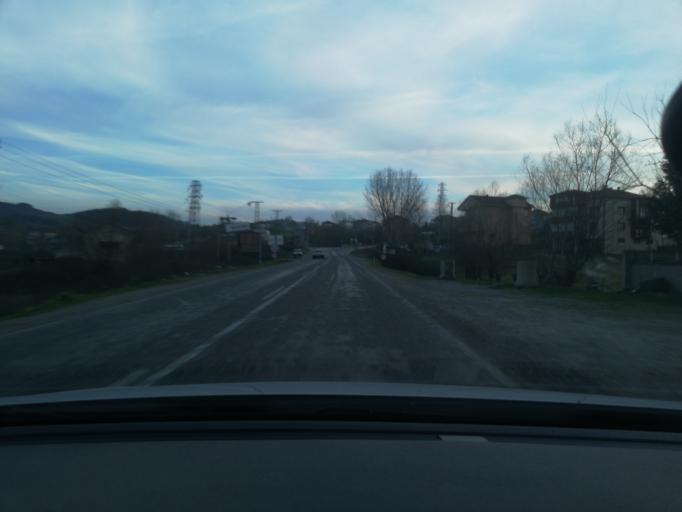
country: TR
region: Zonguldak
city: Saltukova
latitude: 41.5025
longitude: 32.0978
